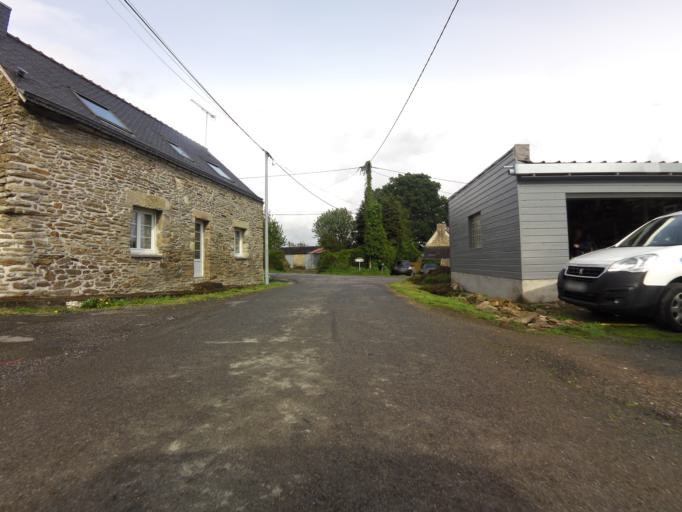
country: FR
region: Brittany
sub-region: Departement du Morbihan
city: Pluherlin
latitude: 47.7133
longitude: -2.3574
